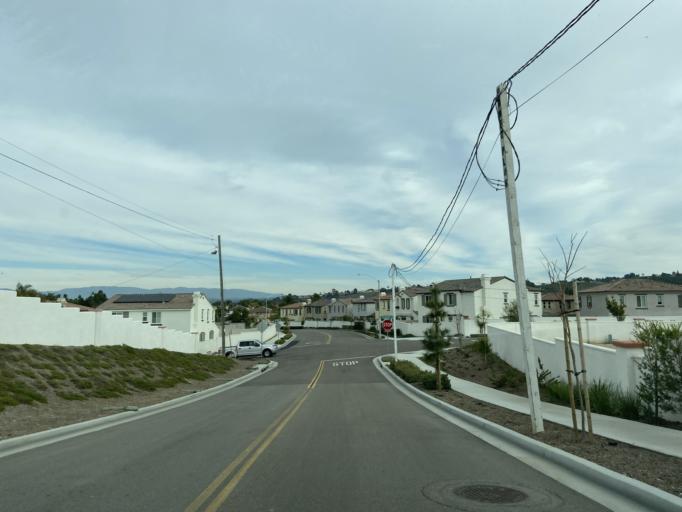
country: US
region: California
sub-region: San Diego County
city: Camp Pendleton South
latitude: 33.2338
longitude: -117.3144
